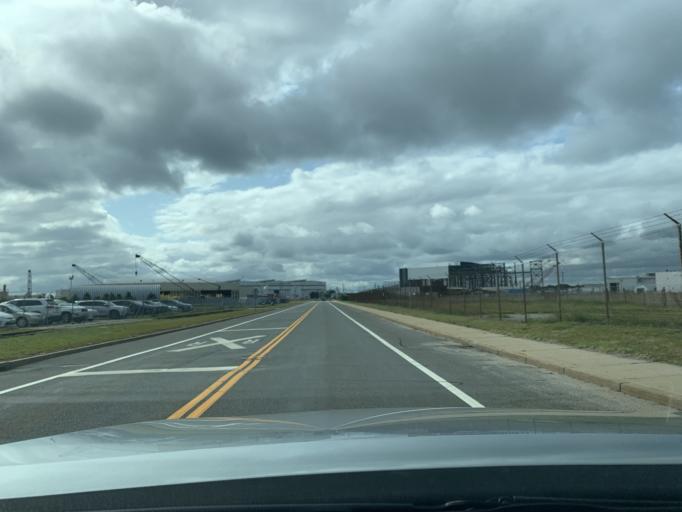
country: US
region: Rhode Island
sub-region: Washington County
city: North Kingstown
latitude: 41.5878
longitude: -71.4142
